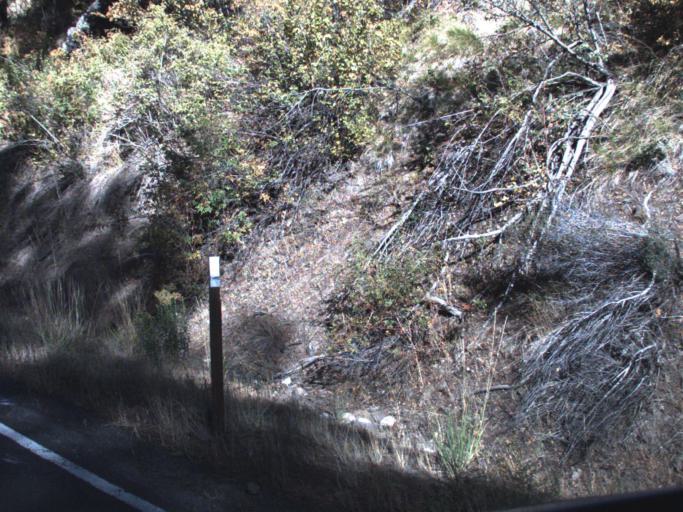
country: US
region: Washington
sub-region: Yakima County
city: Tieton
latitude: 46.6755
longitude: -121.0634
